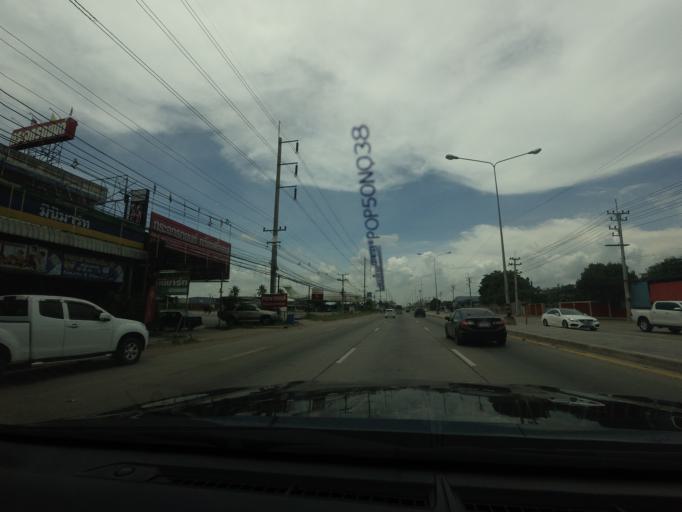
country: TH
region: Nakhon Pathom
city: Nakhon Pathom
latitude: 13.8483
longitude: 100.0213
